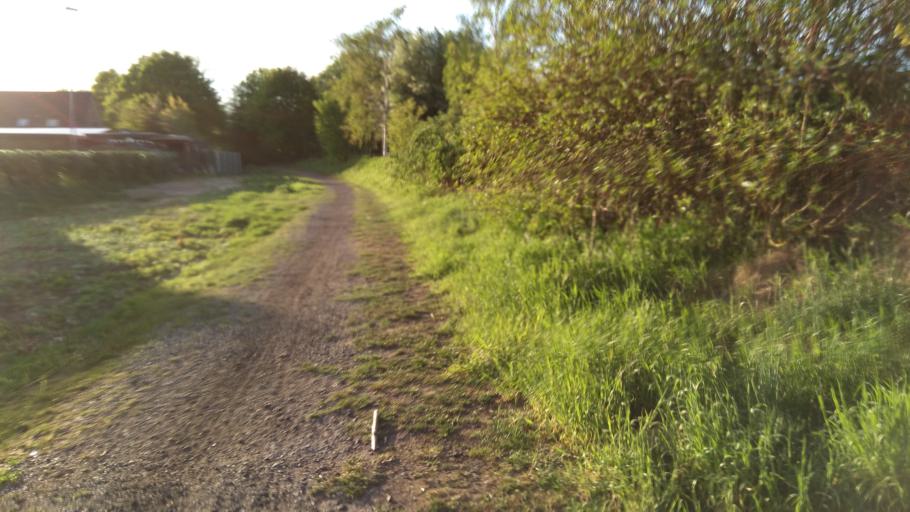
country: DE
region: Lower Saxony
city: Buxtehude
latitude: 53.4681
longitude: 9.7028
